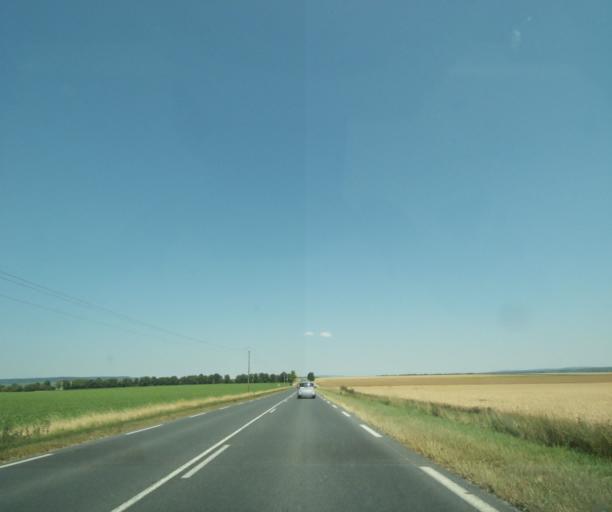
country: FR
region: Champagne-Ardenne
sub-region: Departement de la Marne
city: Mourmelon-le-Grand
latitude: 49.0833
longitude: 4.2802
